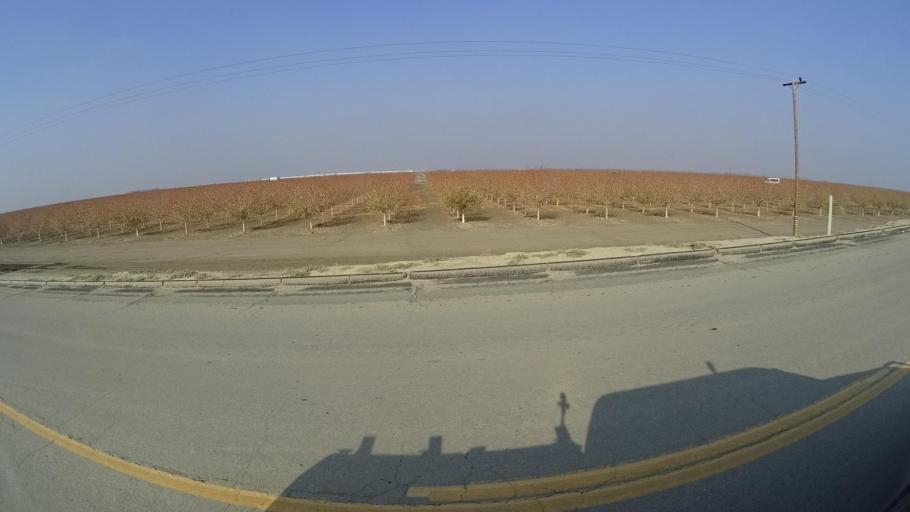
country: US
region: California
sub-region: Kern County
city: Greenfield
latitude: 35.1518
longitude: -119.1020
